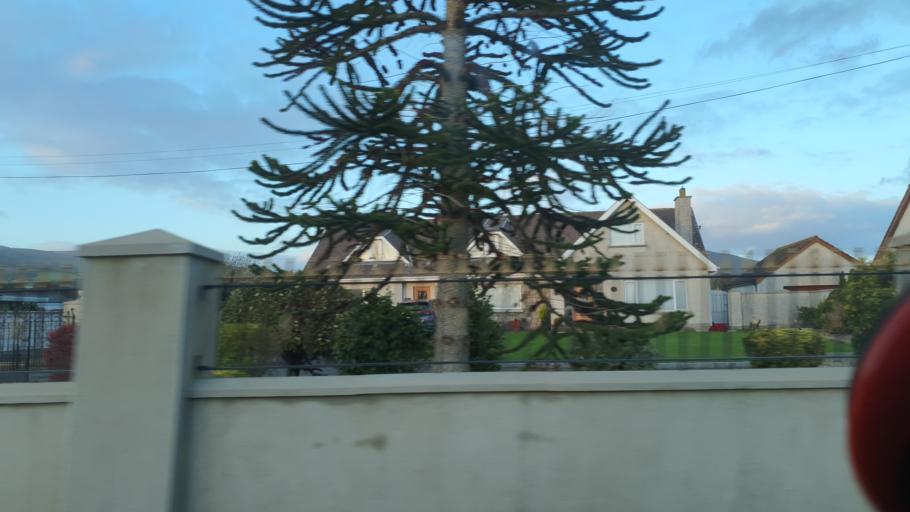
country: GB
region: Northern Ireland
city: Kilkeel
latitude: 54.0633
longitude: -6.0957
